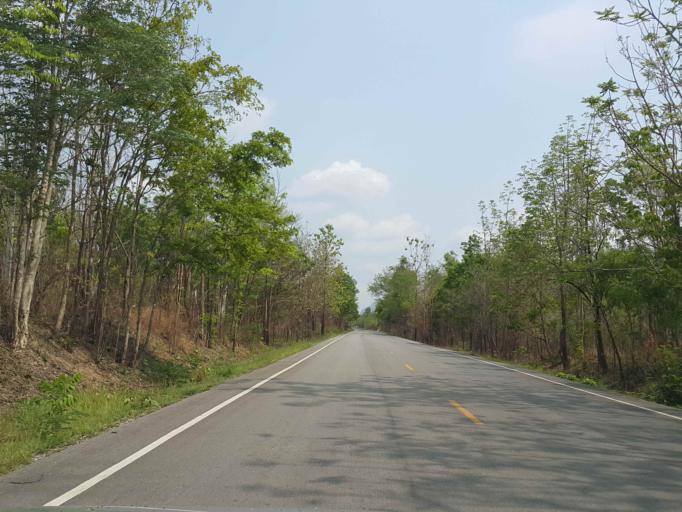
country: TH
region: Sukhothai
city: Thung Saliam
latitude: 17.3710
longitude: 99.4052
